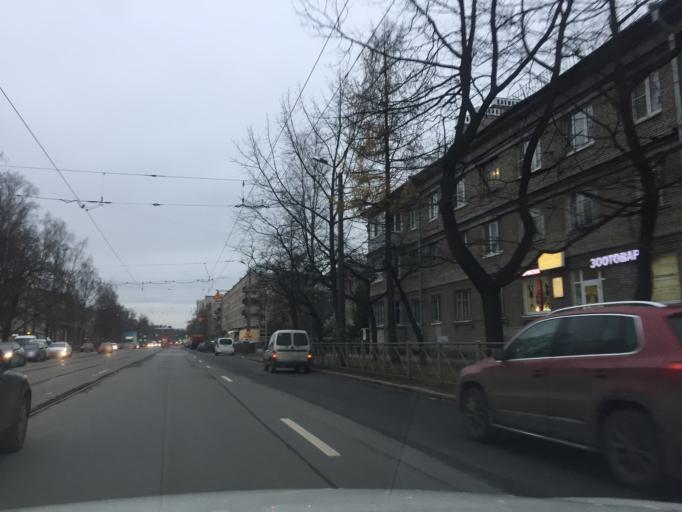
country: RU
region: St.-Petersburg
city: Sosnovka
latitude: 60.0160
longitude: 30.3677
